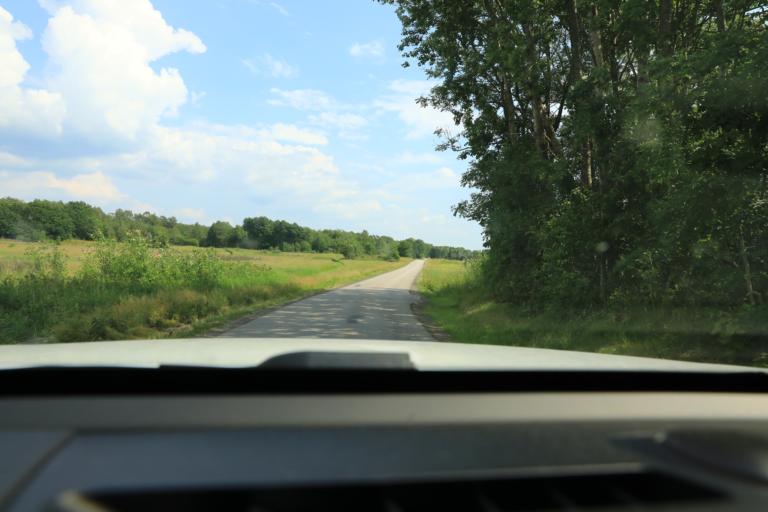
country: SE
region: Halland
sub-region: Varbergs Kommun
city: Varberg
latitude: 57.1577
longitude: 12.3157
